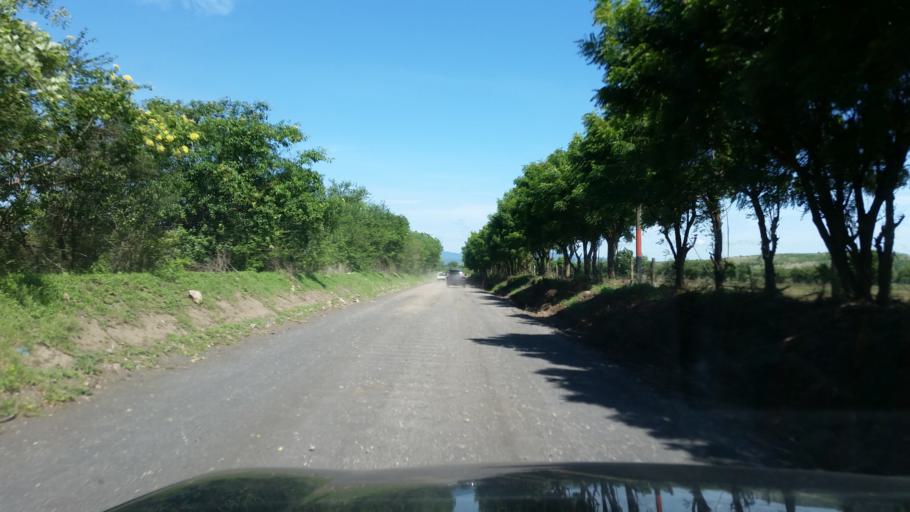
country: NI
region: Chinandega
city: Puerto Morazan
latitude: 12.7704
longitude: -87.0825
